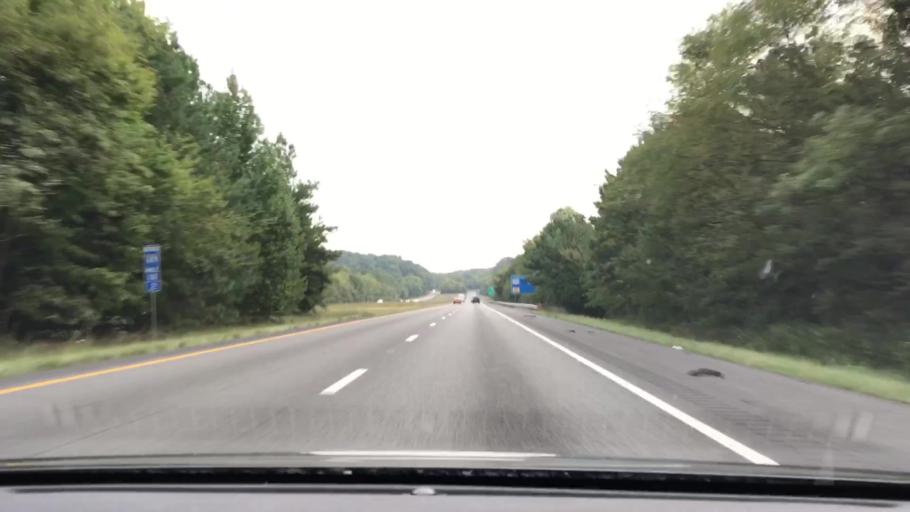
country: US
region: Tennessee
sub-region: Robertson County
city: Cross Plains
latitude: 36.5742
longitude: -86.6161
